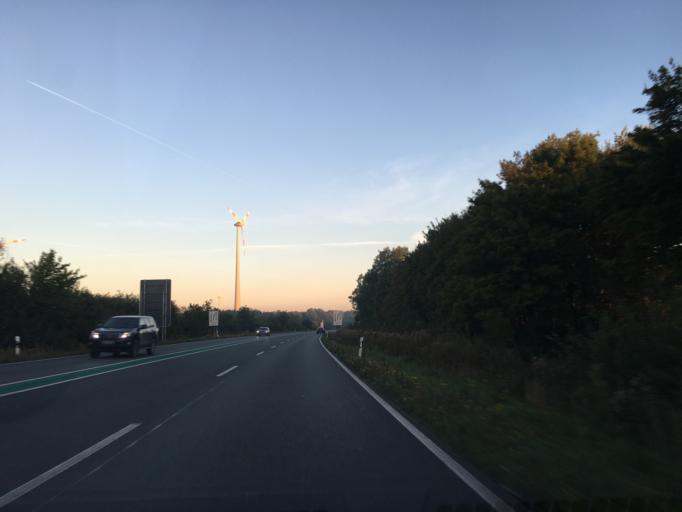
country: DE
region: North Rhine-Westphalia
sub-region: Regierungsbezirk Munster
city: Altenberge
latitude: 52.0777
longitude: 7.4229
